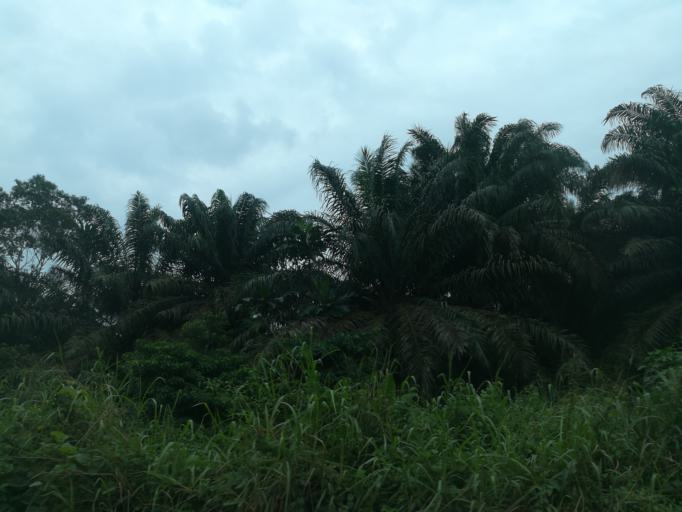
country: NG
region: Lagos
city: Ejirin
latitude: 6.6524
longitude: 3.7929
